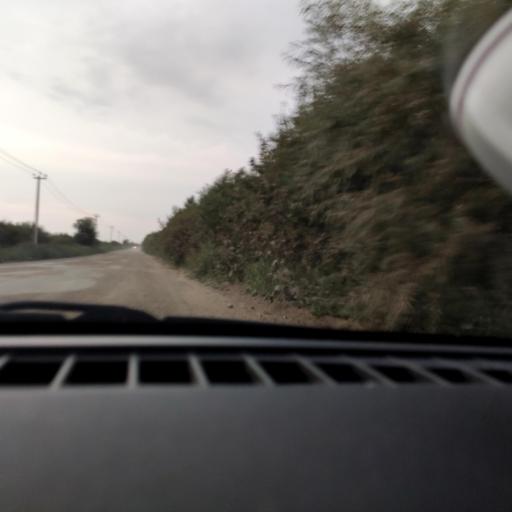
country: RU
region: Perm
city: Kondratovo
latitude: 58.0030
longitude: 56.0219
